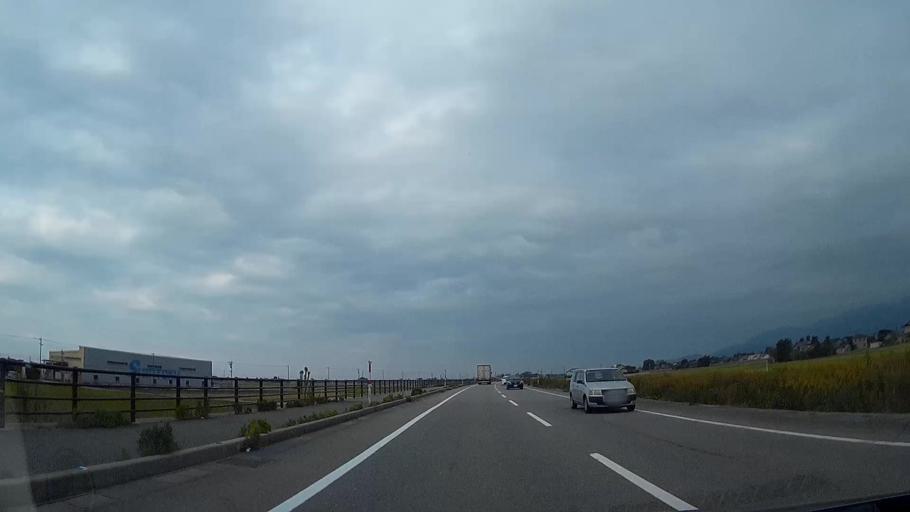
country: JP
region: Toyama
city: Nyuzen
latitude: 36.9241
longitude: 137.4702
